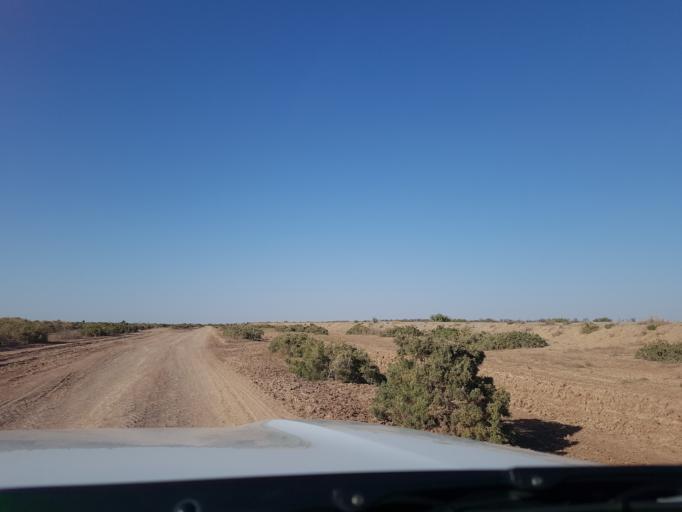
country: IR
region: Razavi Khorasan
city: Sarakhs
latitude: 36.9840
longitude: 61.3866
